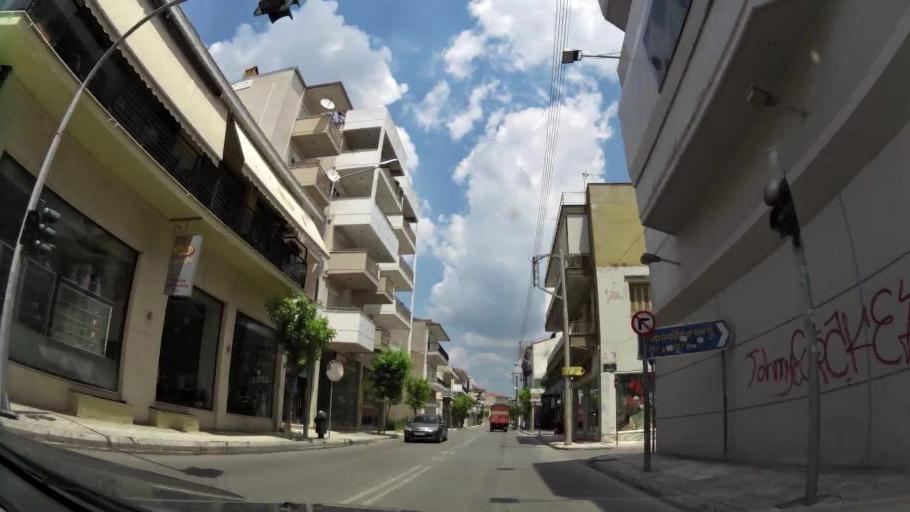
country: GR
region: West Macedonia
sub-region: Nomos Kozanis
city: Kozani
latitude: 40.2982
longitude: 21.7943
